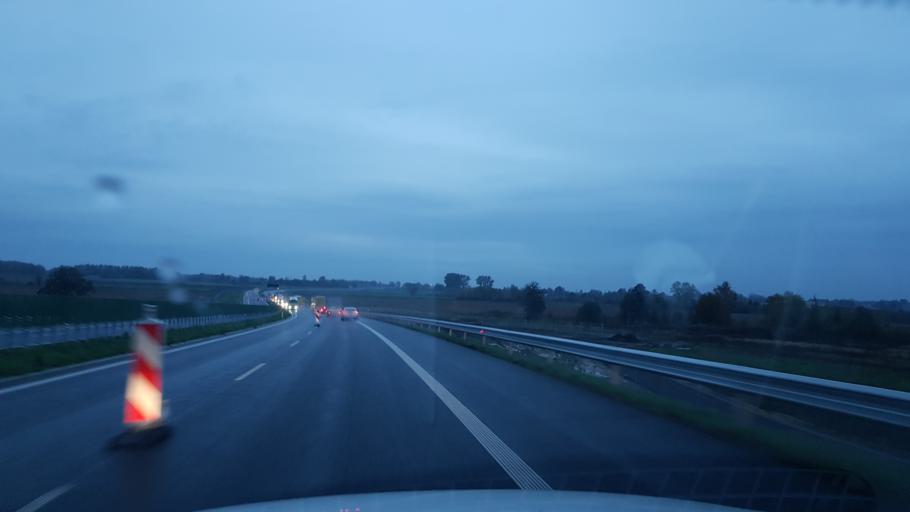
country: PL
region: West Pomeranian Voivodeship
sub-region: Powiat gryficki
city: Ploty
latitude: 53.8001
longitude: 15.2528
